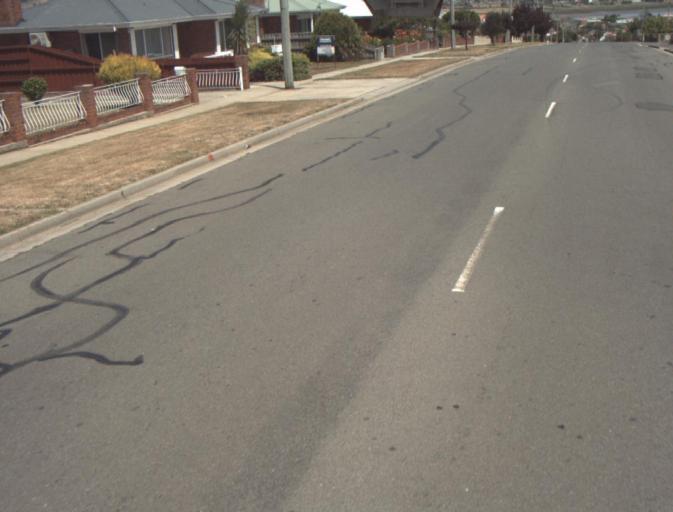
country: AU
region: Tasmania
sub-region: Launceston
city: Mayfield
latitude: -41.3855
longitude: 147.1257
